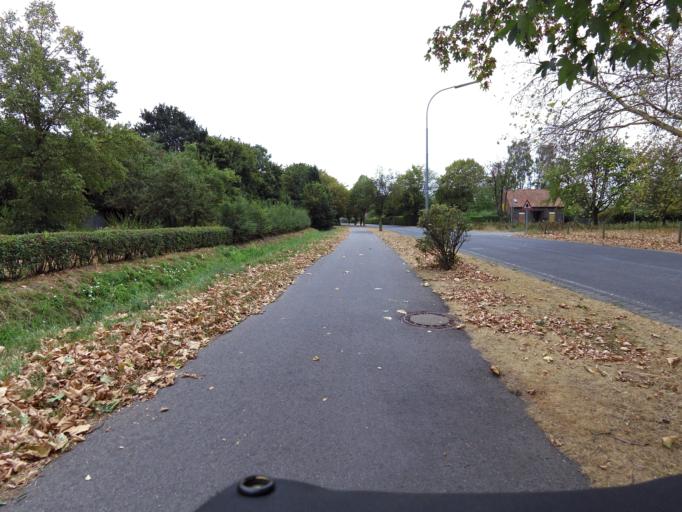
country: DE
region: North Rhine-Westphalia
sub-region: Regierungsbezirk Dusseldorf
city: Kevelaer
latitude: 51.5801
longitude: 6.2313
